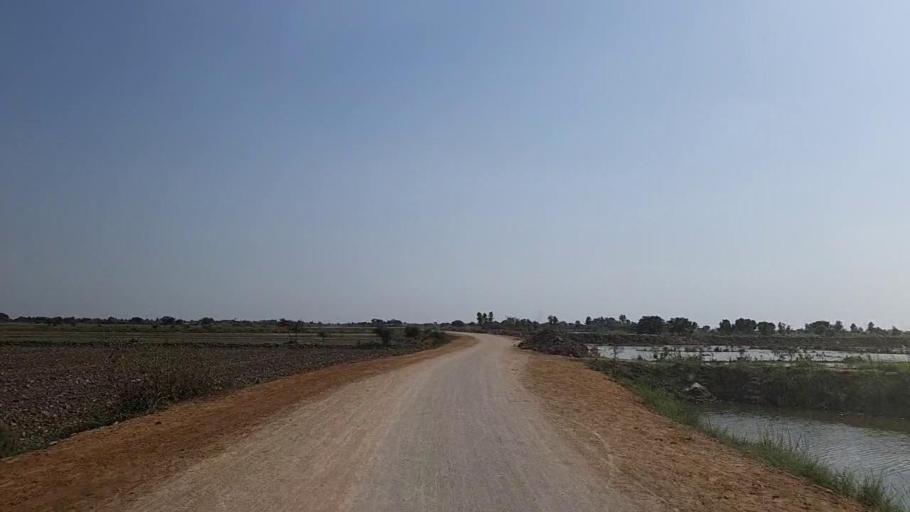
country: PK
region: Sindh
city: Daro Mehar
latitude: 24.7634
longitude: 68.1832
